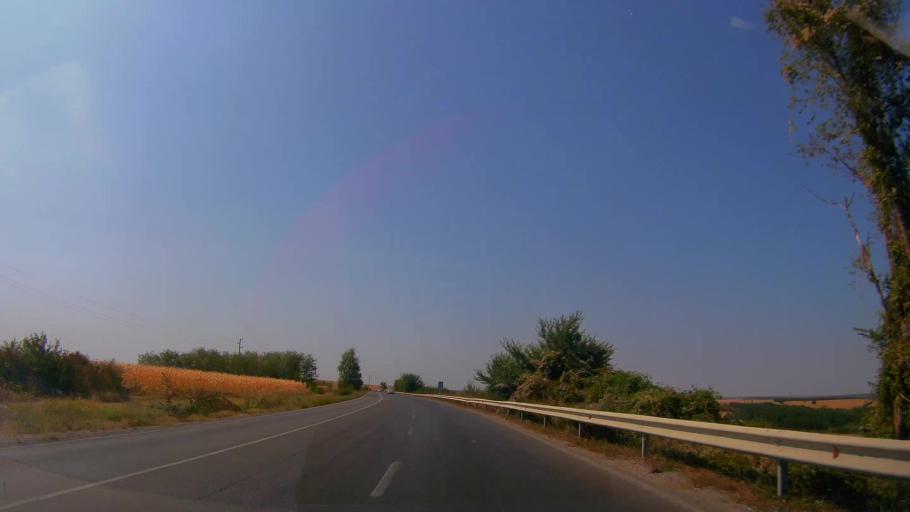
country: BG
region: Ruse
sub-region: Obshtina Vetovo
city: Senovo
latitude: 43.5621
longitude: 26.3592
